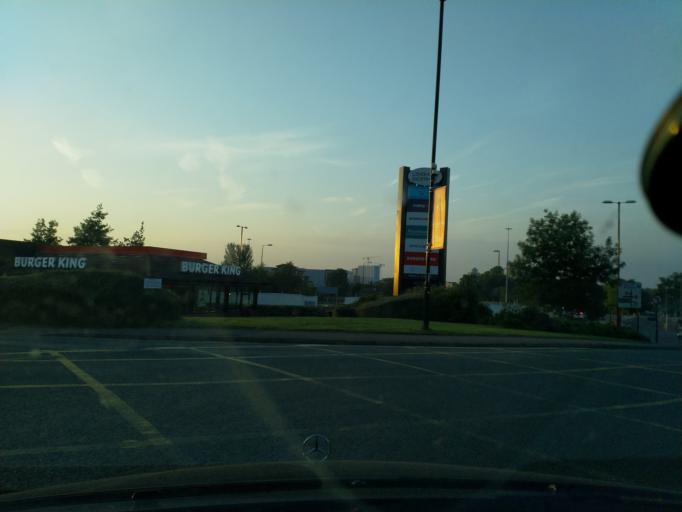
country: GB
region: England
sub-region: Coventry
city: Coventry
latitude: 52.4017
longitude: -1.5158
